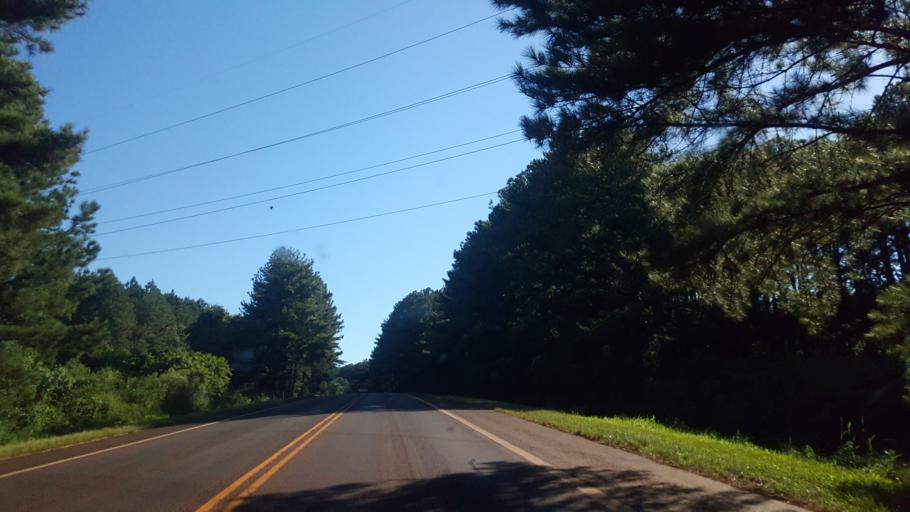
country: AR
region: Misiones
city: Puerto Libertad
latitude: -25.9052
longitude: -54.5652
